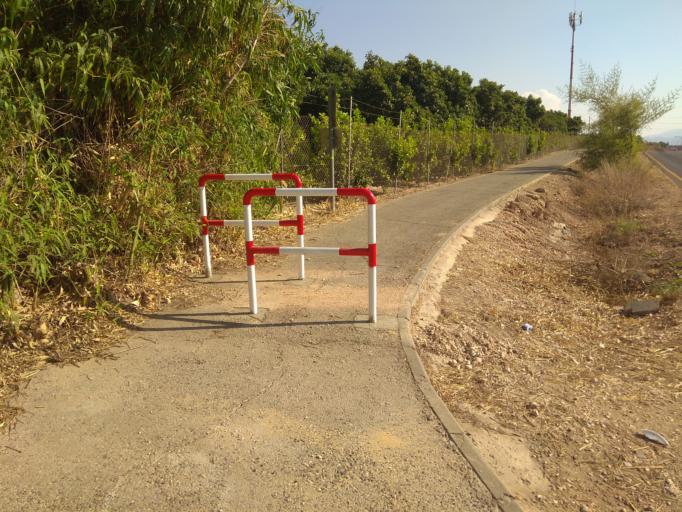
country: IL
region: Northern District
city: Qiryat Shemona
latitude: 33.2272
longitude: 35.6230
